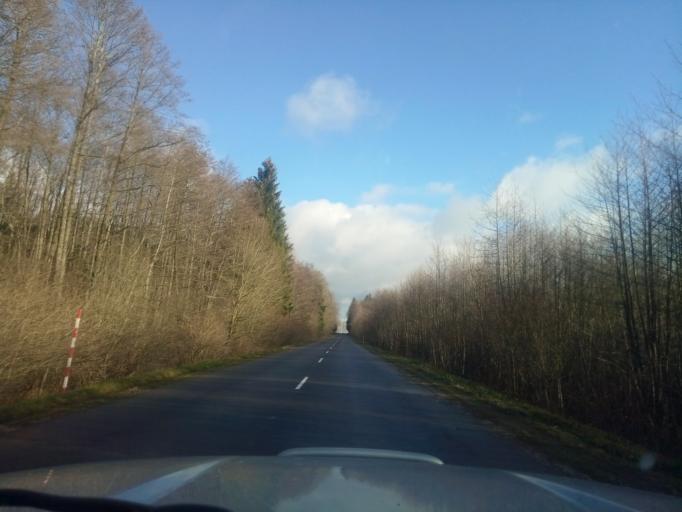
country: BY
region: Minsk
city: Tsimkavichy
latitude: 53.1708
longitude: 26.9278
